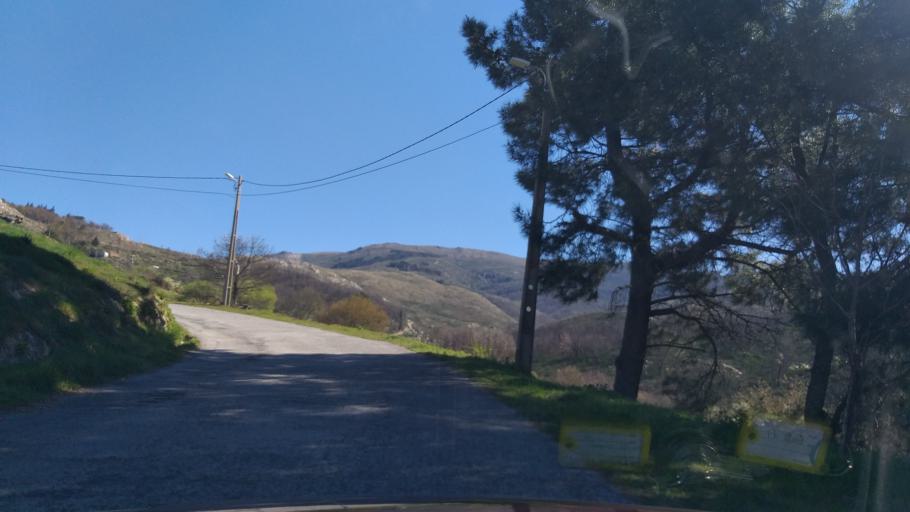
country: PT
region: Guarda
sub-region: Manteigas
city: Manteigas
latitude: 40.4900
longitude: -7.5858
